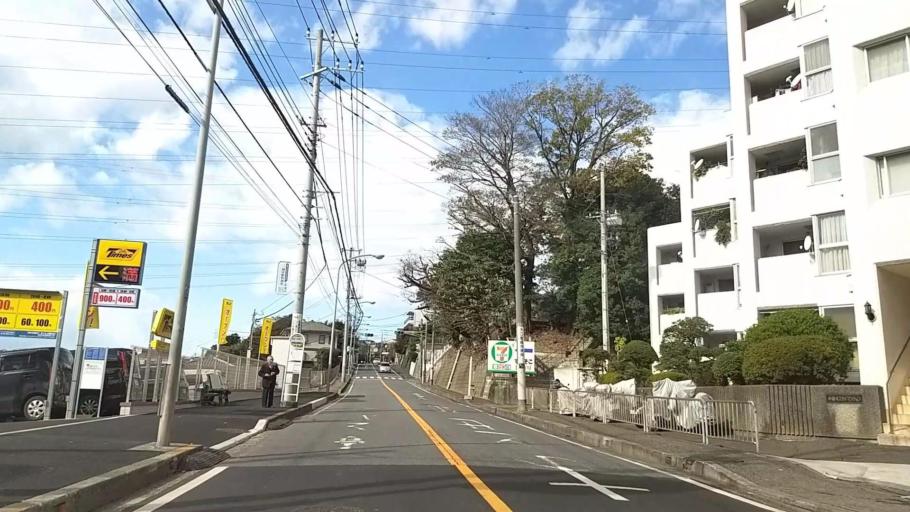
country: JP
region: Kanagawa
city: Yokohama
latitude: 35.4914
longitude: 139.6379
